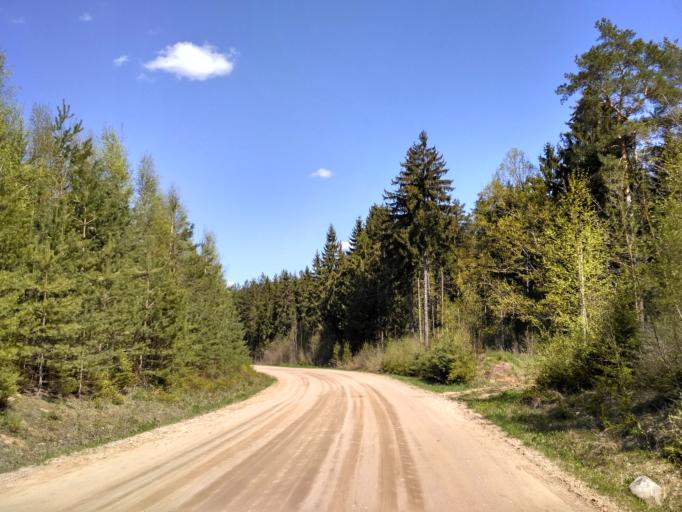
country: BY
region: Minsk
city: Horad Barysaw
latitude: 54.4192
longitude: 28.4641
